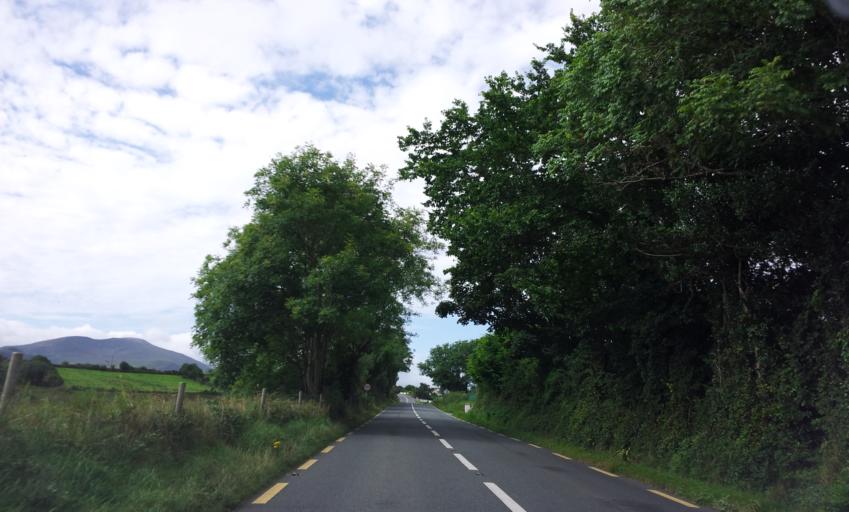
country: IE
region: Munster
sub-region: Ciarrai
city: Killorglin
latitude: 52.0948
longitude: -9.8391
